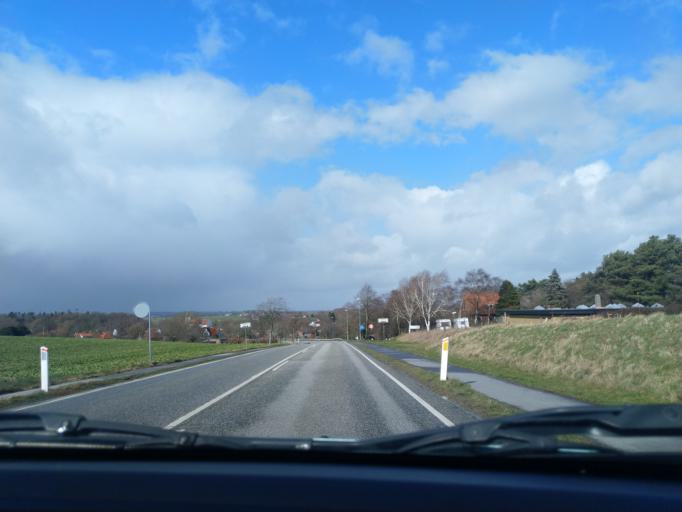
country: DK
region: Zealand
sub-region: Naestved Kommune
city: Naestved
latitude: 55.3119
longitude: 11.6844
